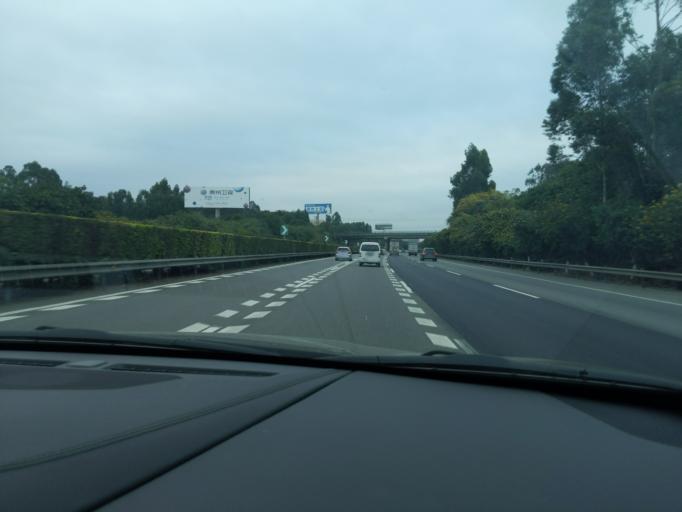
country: CN
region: Fujian
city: Neikeng
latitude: 24.7718
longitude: 118.4544
